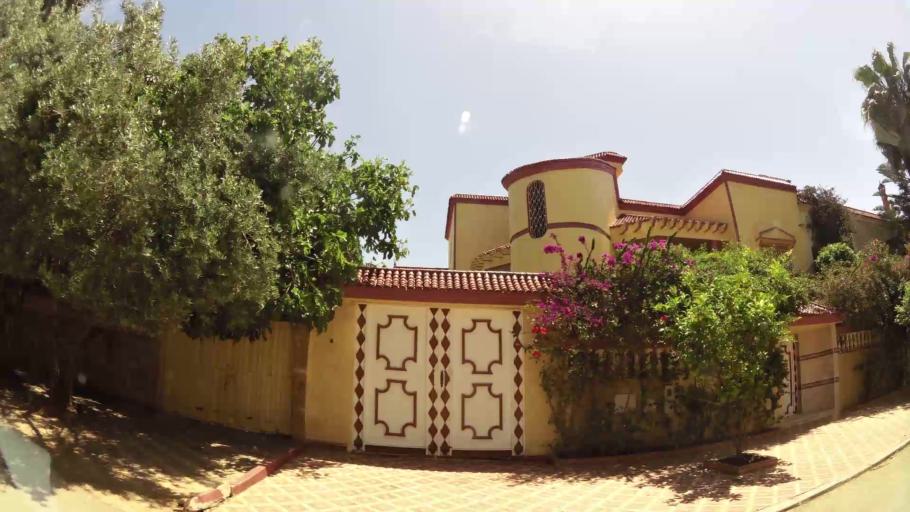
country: MA
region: Rabat-Sale-Zemmour-Zaer
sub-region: Khemisset
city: Khemisset
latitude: 33.8287
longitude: -6.0889
